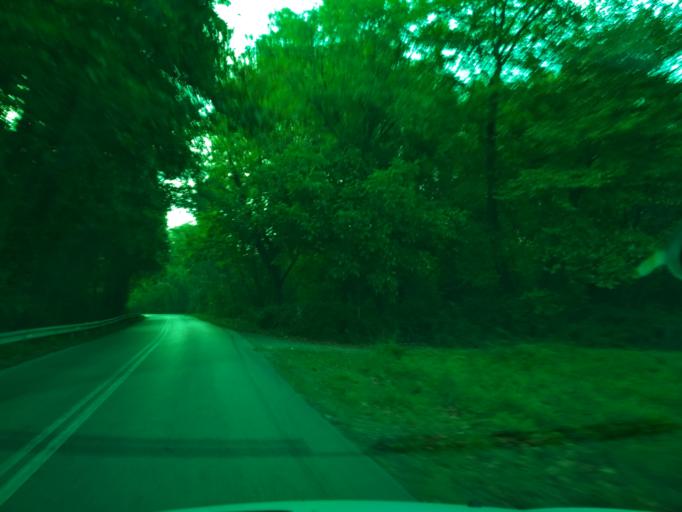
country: GR
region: Central Greece
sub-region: Nomos Evvoias
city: Prokopion
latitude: 38.7504
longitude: 23.4856
